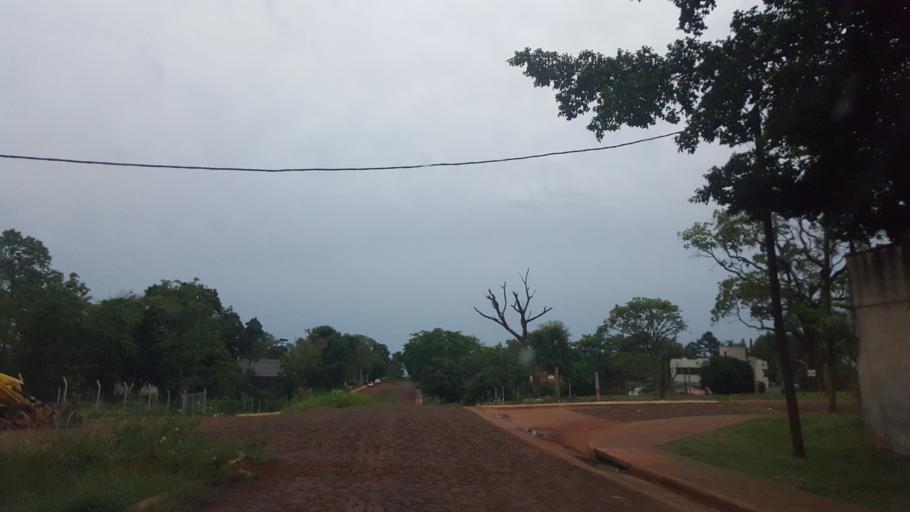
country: AR
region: Misiones
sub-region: Departamento de Capital
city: Posadas
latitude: -27.3575
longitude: -55.9227
